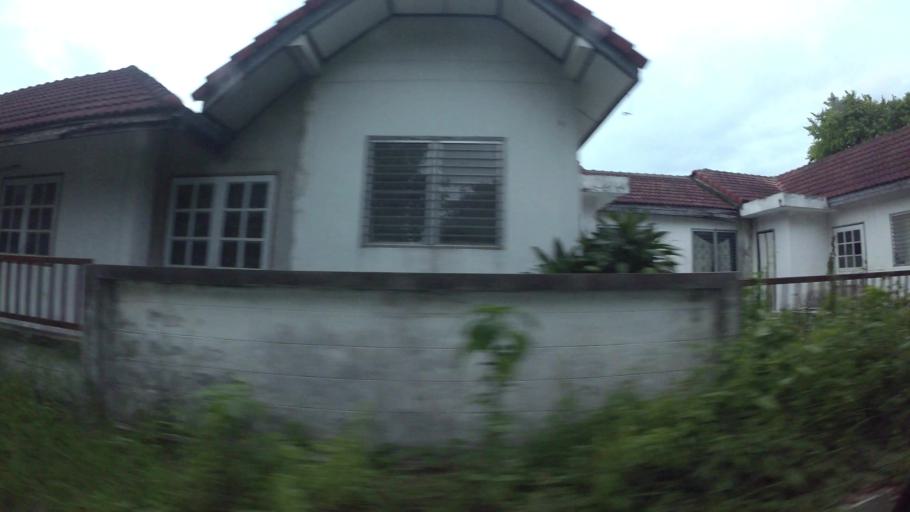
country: TH
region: Chon Buri
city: Sattahip
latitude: 12.6939
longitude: 100.8999
